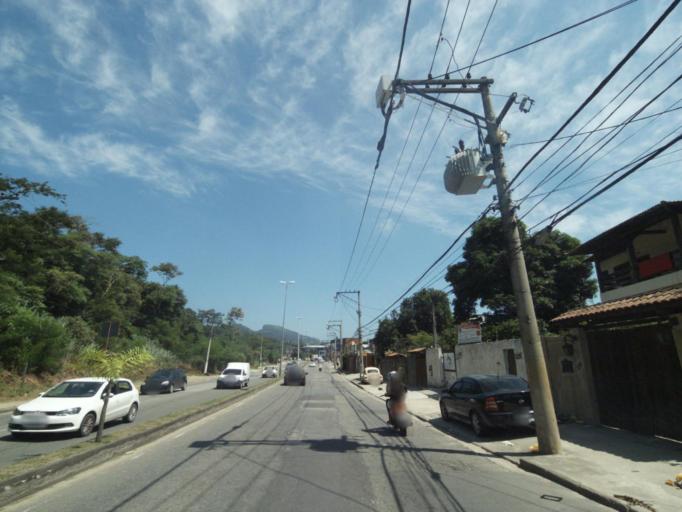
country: BR
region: Rio de Janeiro
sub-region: Sao Goncalo
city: Sao Goncalo
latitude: -22.8857
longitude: -43.0325
